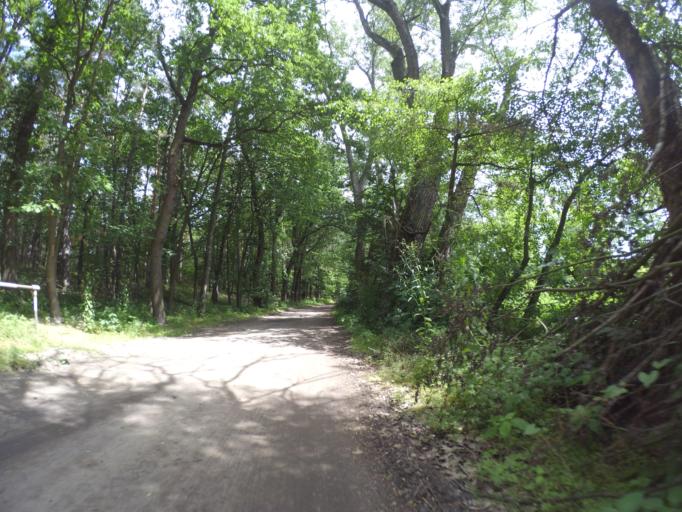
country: CZ
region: Central Bohemia
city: Prerov nad Labem
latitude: 50.1837
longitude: 14.8107
